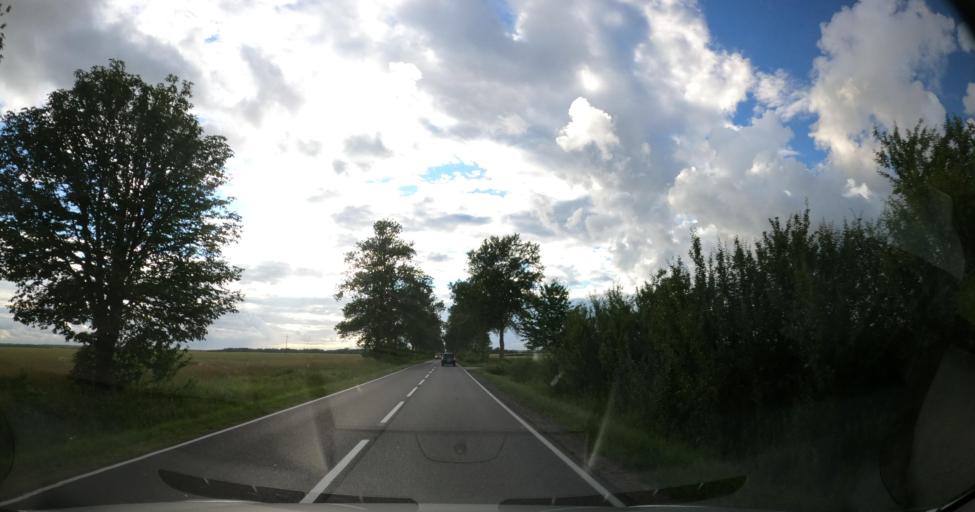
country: PL
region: Pomeranian Voivodeship
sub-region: Powiat slupski
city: Potegowo
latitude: 54.4240
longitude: 17.3761
